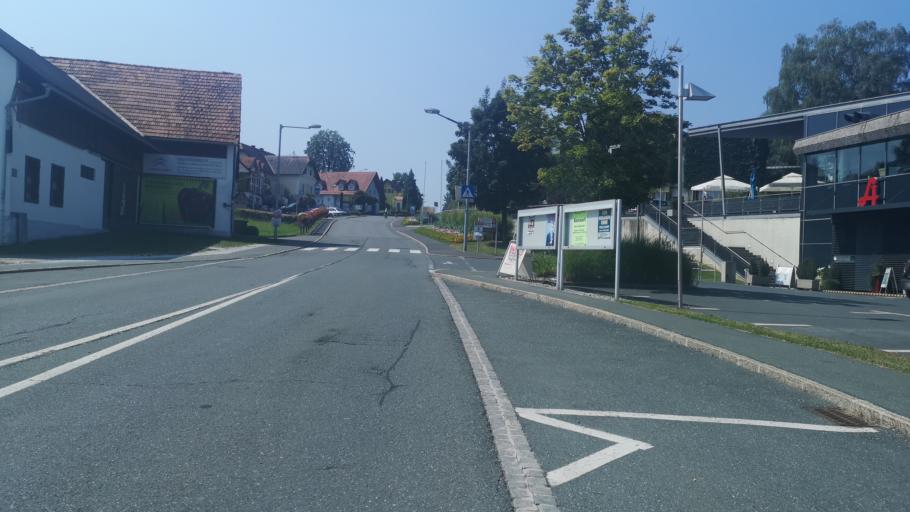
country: AT
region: Styria
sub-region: Politischer Bezirk Deutschlandsberg
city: Lannach
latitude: 46.9460
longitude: 15.3351
